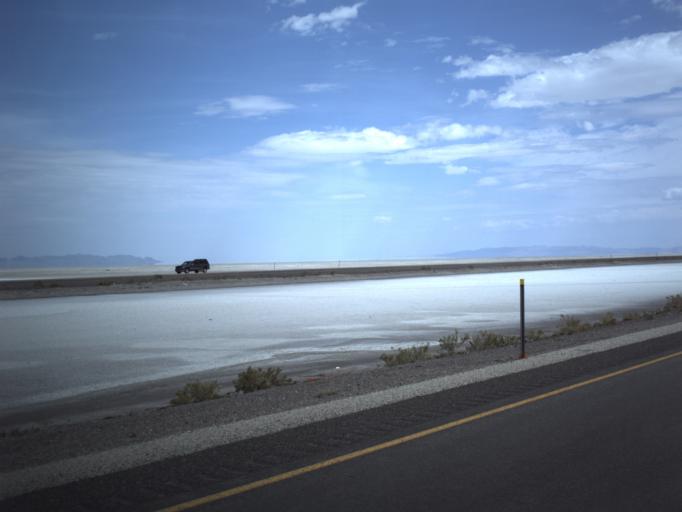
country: US
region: Utah
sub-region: Tooele County
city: Wendover
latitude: 40.7349
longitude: -113.6799
